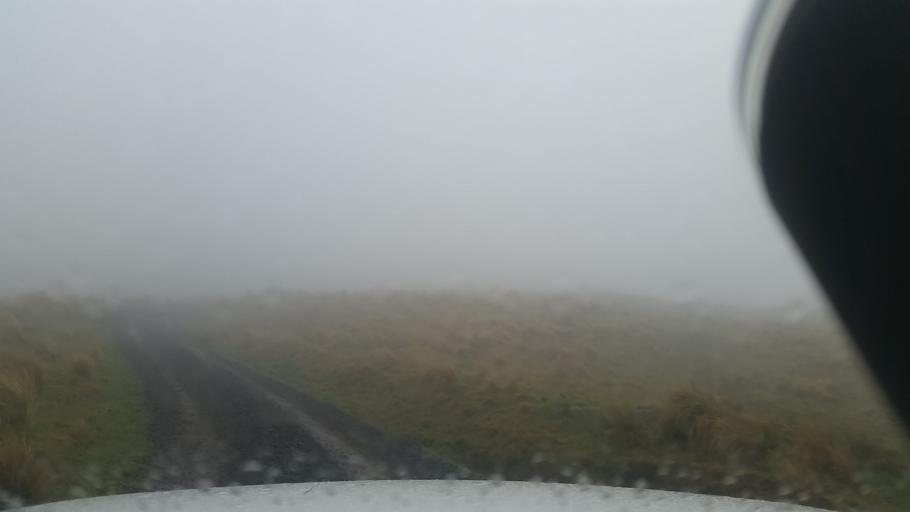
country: NZ
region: Canterbury
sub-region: Christchurch City
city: Christchurch
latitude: -43.8721
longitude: 172.9096
